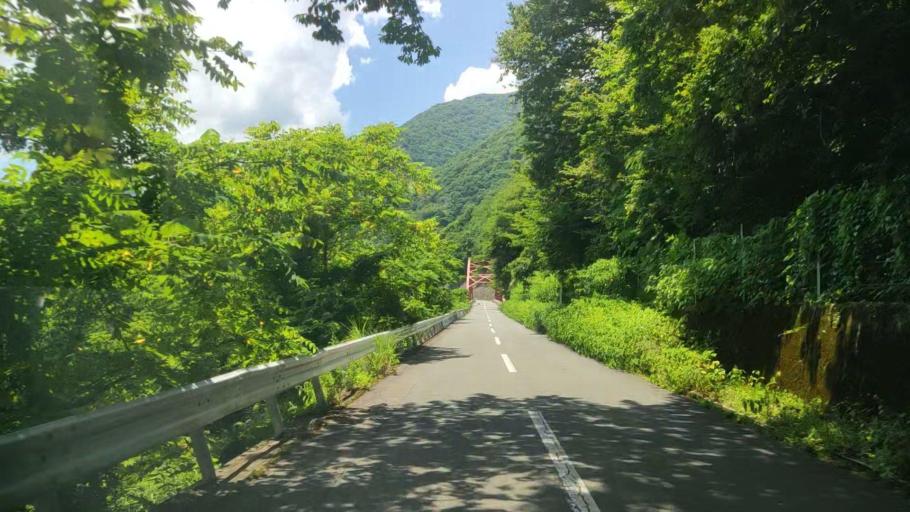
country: JP
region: Fukui
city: Ono
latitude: 35.9003
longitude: 136.5116
